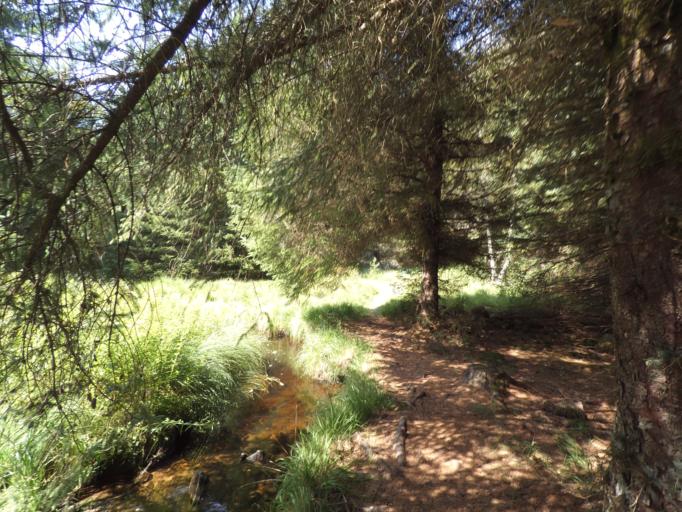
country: FR
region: Limousin
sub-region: Departement de la Correze
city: Bugeat
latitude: 45.6860
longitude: 2.0272
